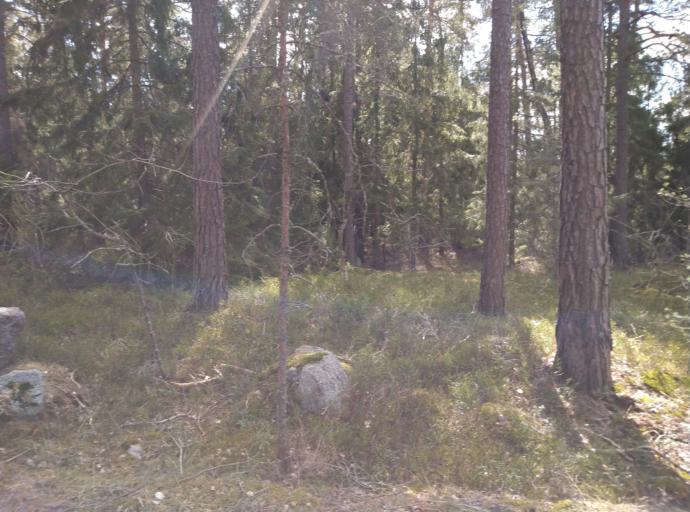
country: SE
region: Stockholm
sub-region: Nacka Kommun
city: Fisksatra
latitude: 59.2940
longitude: 18.2398
